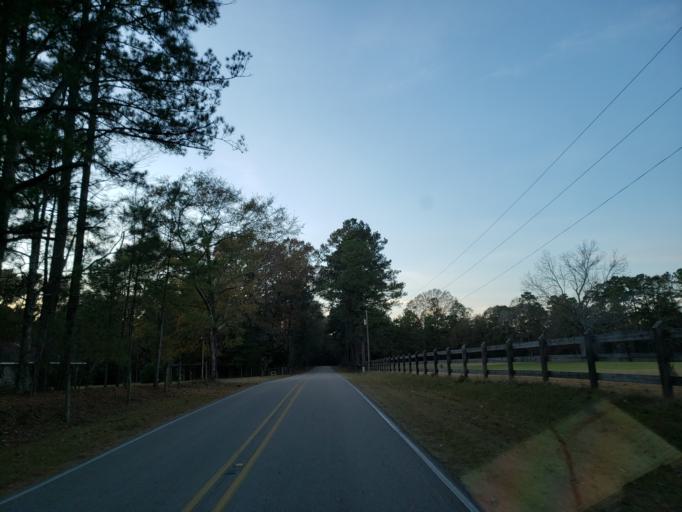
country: US
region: Mississippi
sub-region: Forrest County
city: Hattiesburg
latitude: 31.2417
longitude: -89.3142
